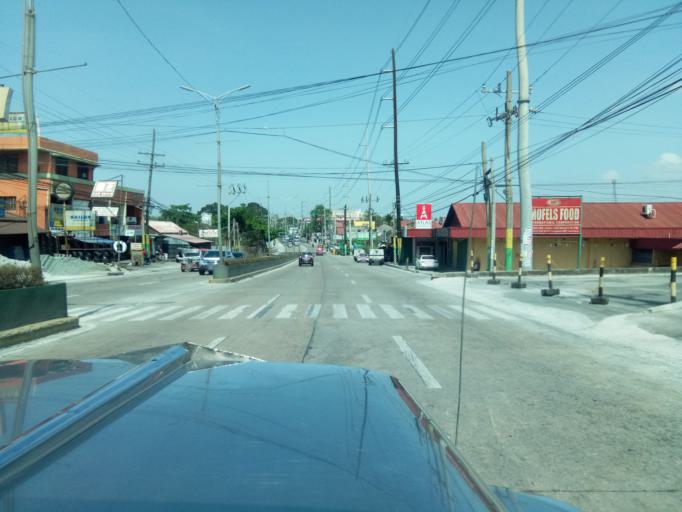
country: PH
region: Calabarzon
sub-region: Province of Cavite
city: Manggahan
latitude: 14.2923
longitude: 120.9337
